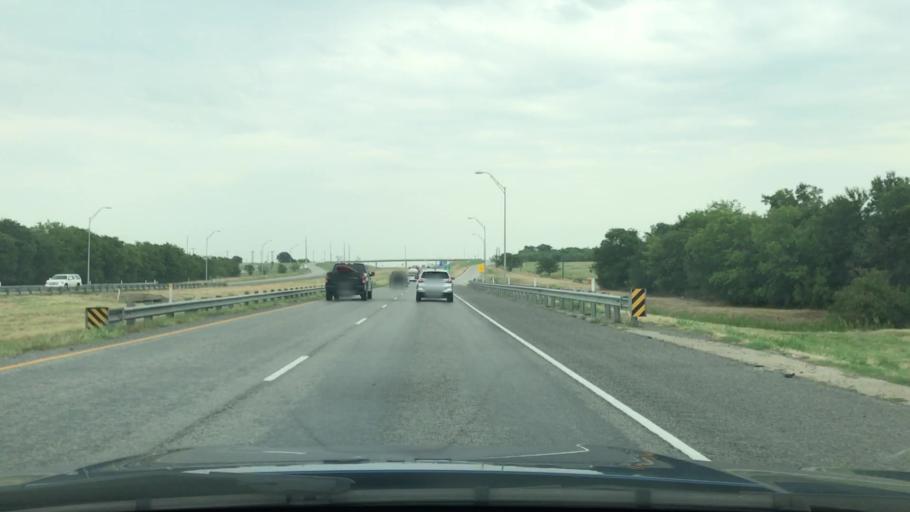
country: US
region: Texas
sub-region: Kaufman County
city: Talty
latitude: 32.7337
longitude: -96.3474
